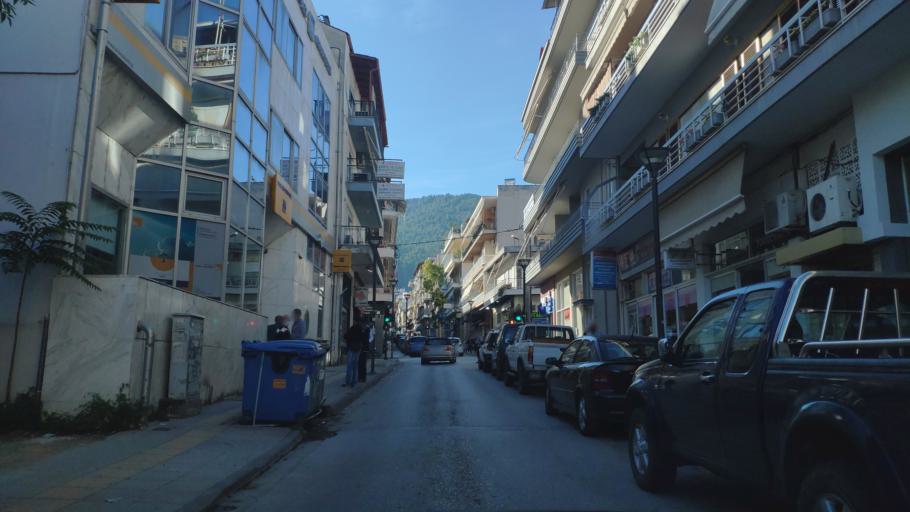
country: GR
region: Central Greece
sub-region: Nomos Voiotias
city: Livadeia
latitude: 38.4397
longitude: 22.8776
